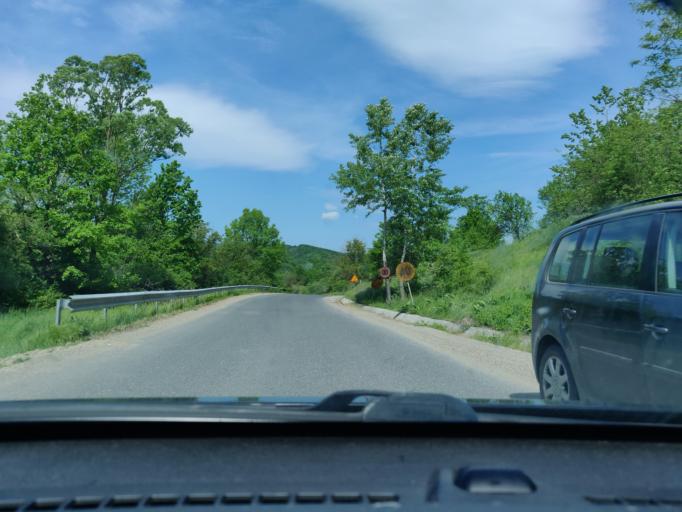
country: RO
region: Vrancea
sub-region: Comuna Vidra
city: Vidra
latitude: 45.9387
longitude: 26.8779
